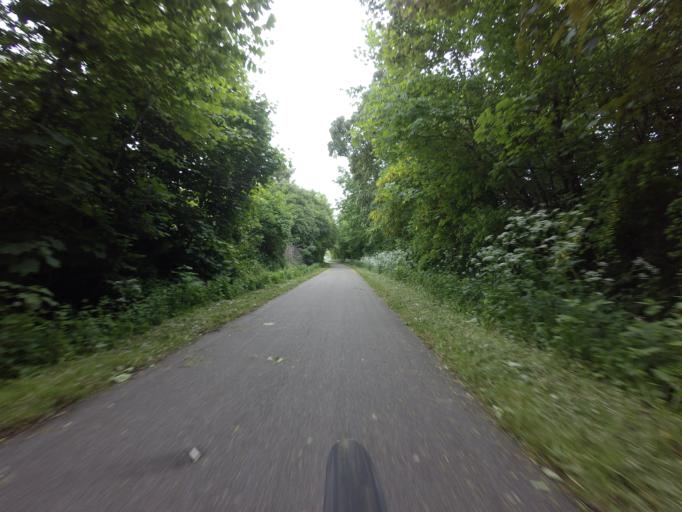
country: DK
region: Zealand
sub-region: Slagelse Kommune
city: Skaelskor
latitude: 55.2458
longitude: 11.3013
